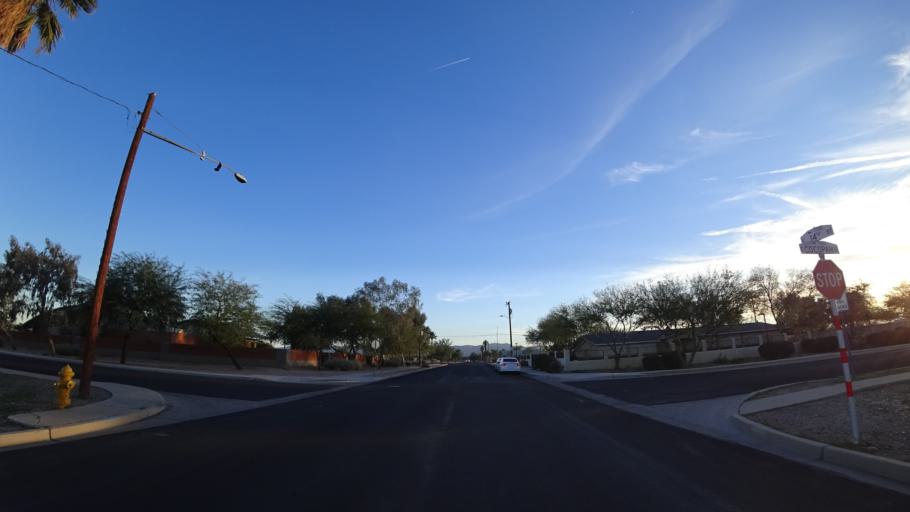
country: US
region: Arizona
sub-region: Maricopa County
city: Phoenix
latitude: 33.4324
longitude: -112.0523
